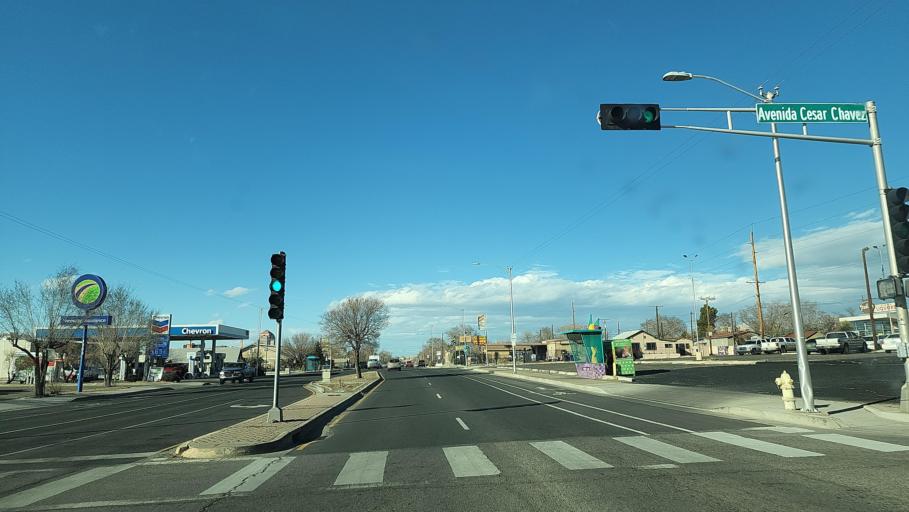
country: US
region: New Mexico
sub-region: Bernalillo County
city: Albuquerque
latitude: 35.0697
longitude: -106.6455
